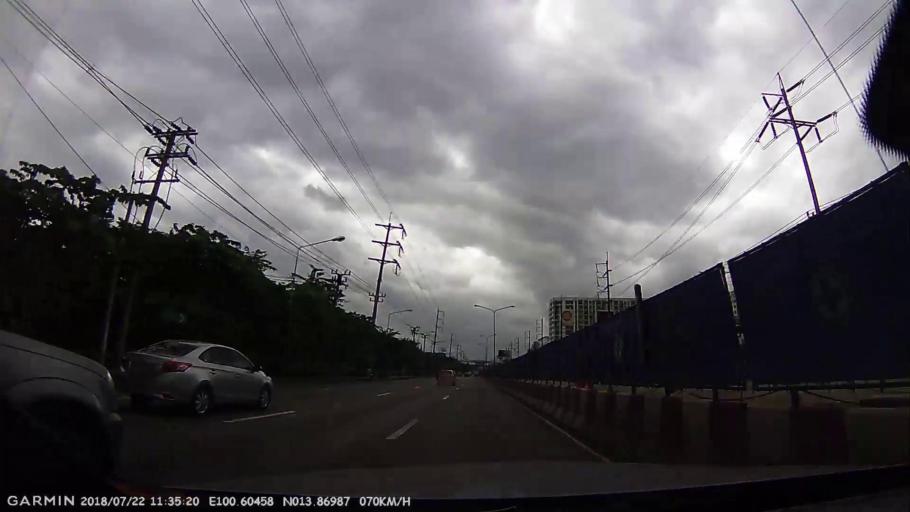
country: TH
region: Bangkok
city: Bang Khen
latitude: 13.8699
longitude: 100.6045
